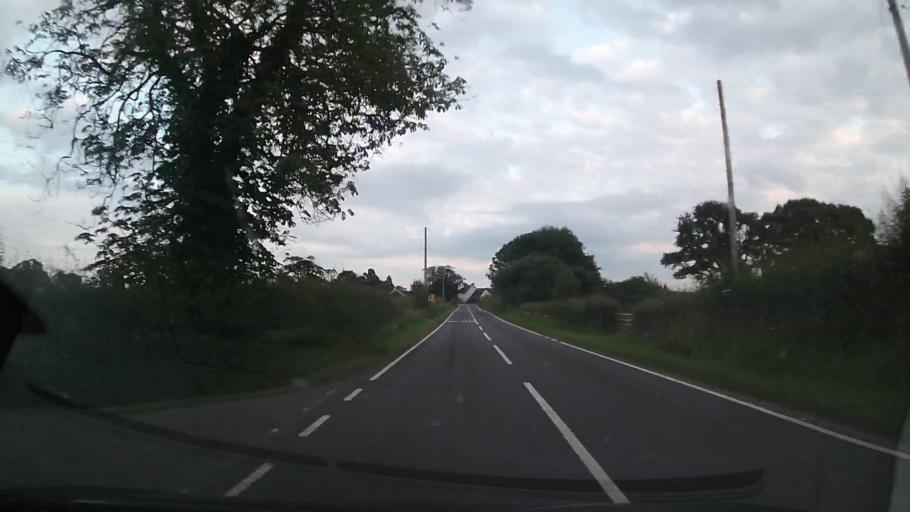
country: GB
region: England
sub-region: Shropshire
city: Petton
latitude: 52.8073
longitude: -2.7983
